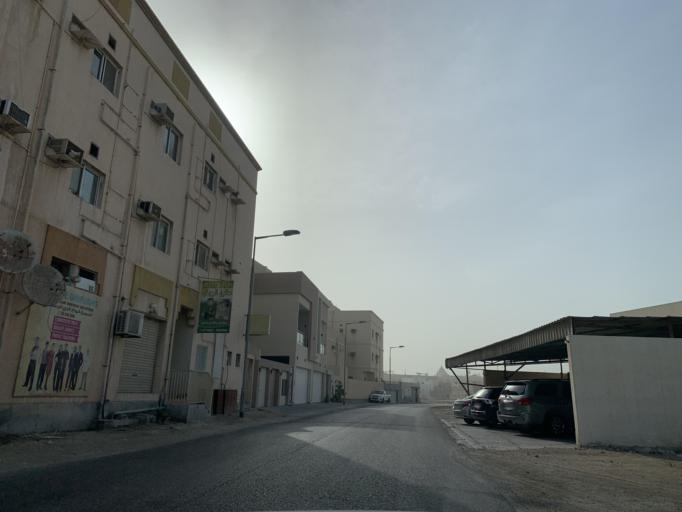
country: BH
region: Northern
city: Madinat `Isa
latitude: 26.1650
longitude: 50.5181
